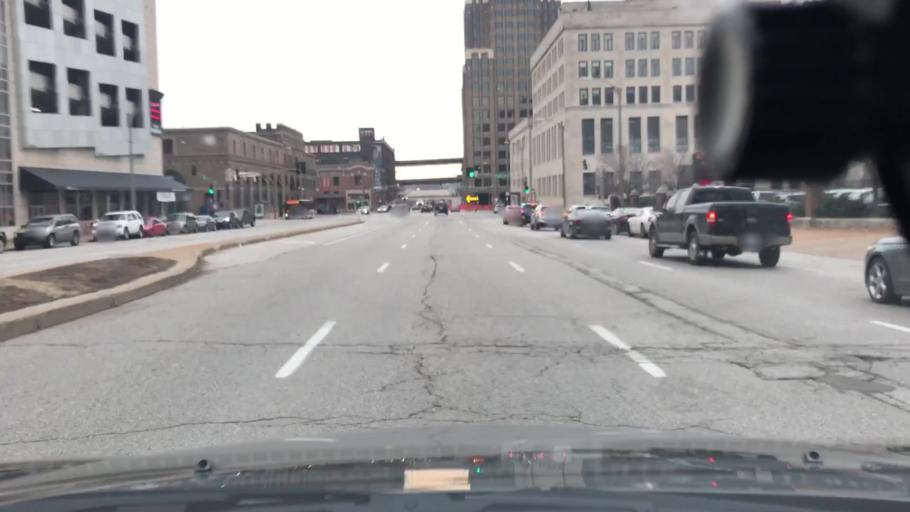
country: US
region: Missouri
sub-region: City of Saint Louis
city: St. Louis
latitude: 38.6261
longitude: -90.1988
